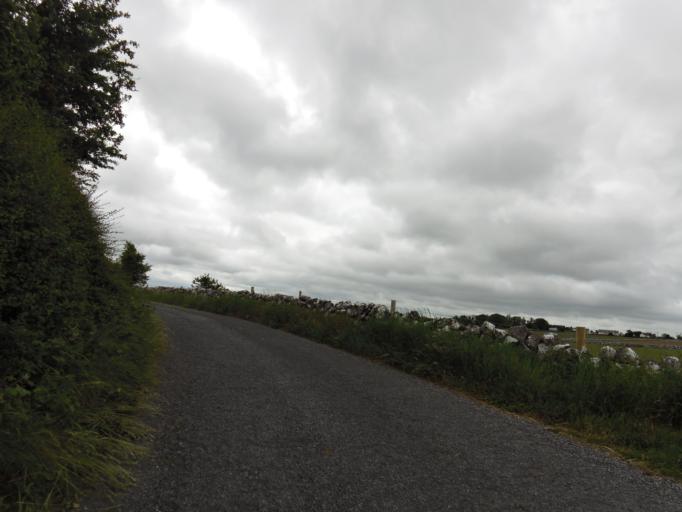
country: IE
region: Connaught
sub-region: County Galway
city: Athenry
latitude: 53.3177
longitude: -8.7229
